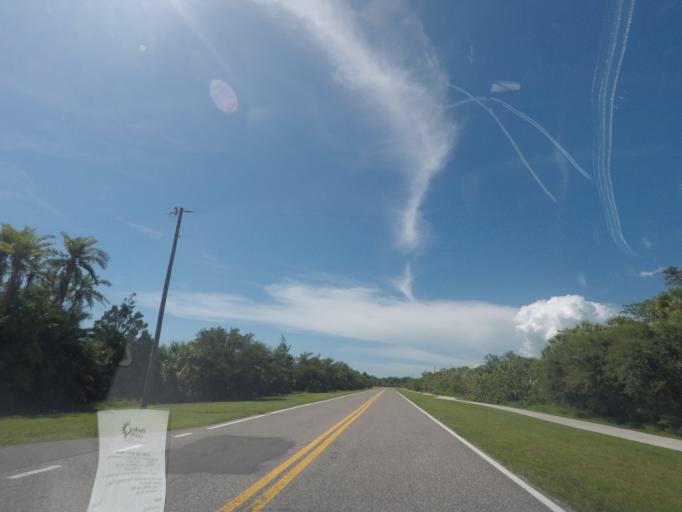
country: US
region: Florida
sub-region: Pinellas County
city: Tierra Verde
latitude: 27.6399
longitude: -82.7377
